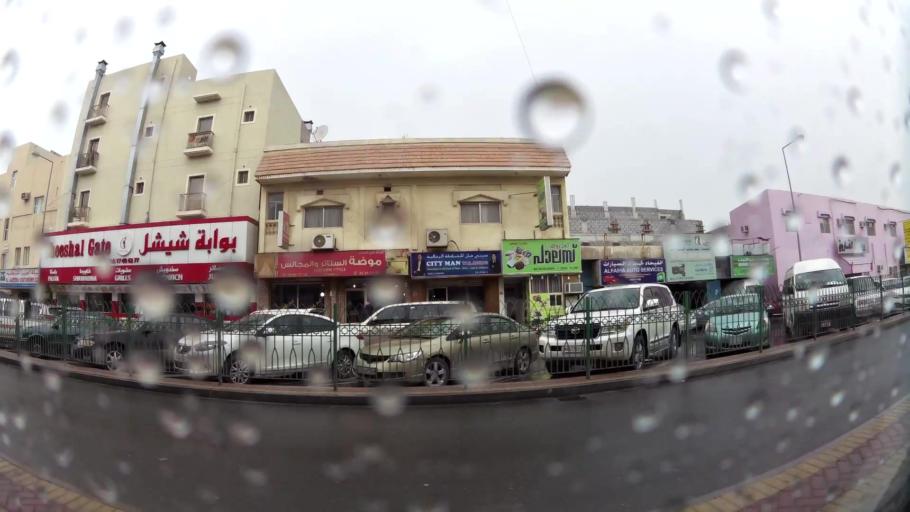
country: BH
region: Northern
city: Madinat `Isa
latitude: 26.1750
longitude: 50.5569
